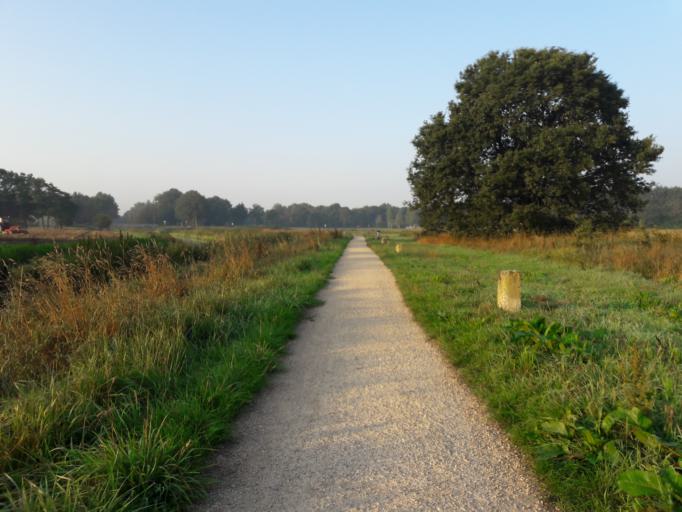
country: NL
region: Drenthe
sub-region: Gemeente Borger-Odoorn
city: Borger
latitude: 52.9279
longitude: 6.8030
